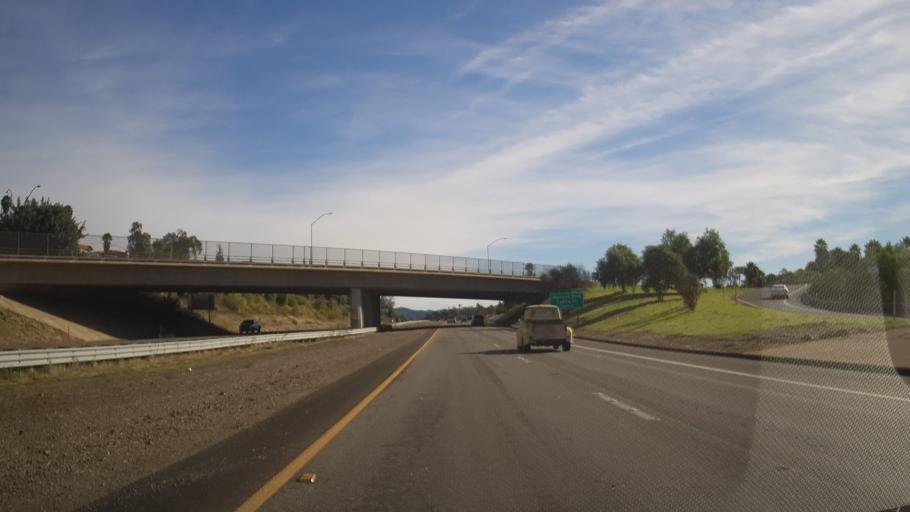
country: US
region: California
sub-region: San Diego County
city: Casa de Oro-Mount Helix
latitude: 32.7432
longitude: -116.9750
